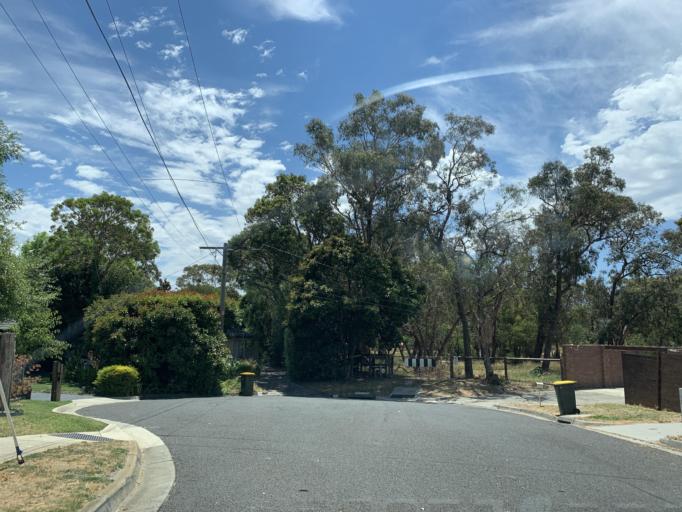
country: AU
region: Victoria
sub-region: Frankston
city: Langwarrin
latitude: -38.1478
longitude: 145.1876
